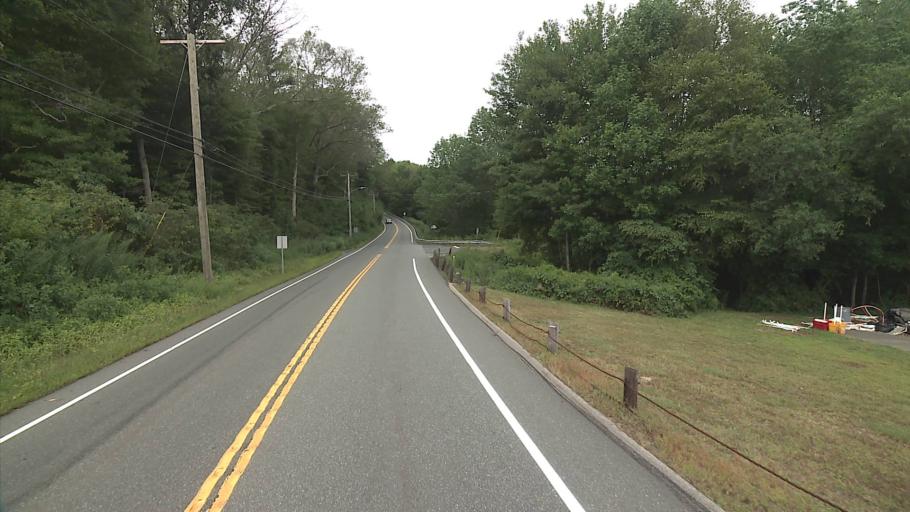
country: US
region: Connecticut
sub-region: New London County
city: Colchester
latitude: 41.5098
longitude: -72.2903
